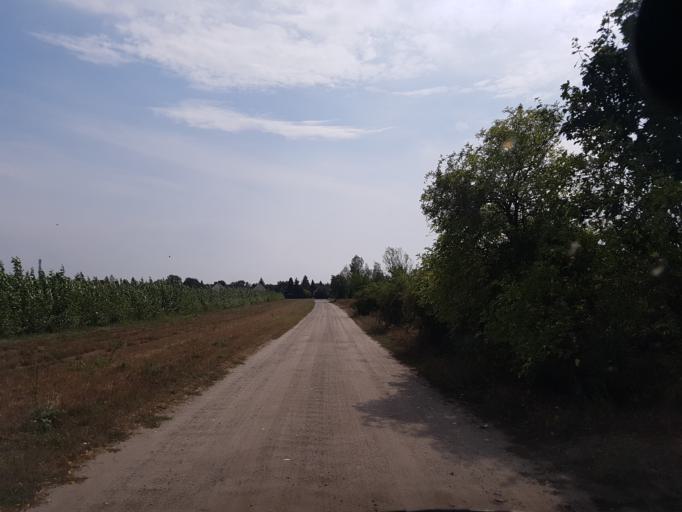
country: DE
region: Brandenburg
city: Finsterwalde
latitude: 51.6464
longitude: 13.7043
